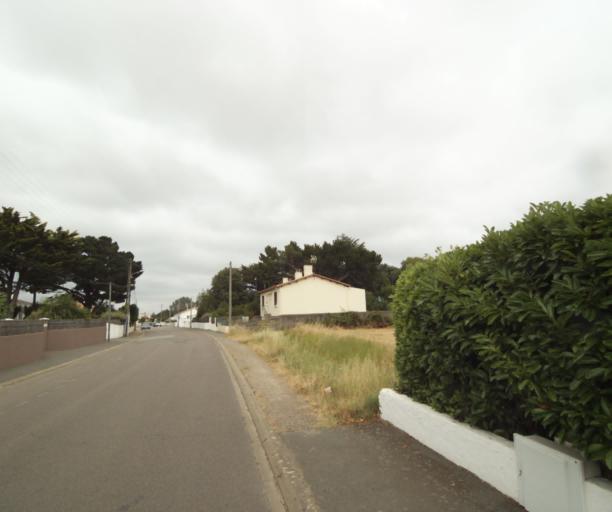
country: FR
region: Pays de la Loire
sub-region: Departement de la Vendee
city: Chateau-d'Olonne
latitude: 46.4979
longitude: -1.7480
